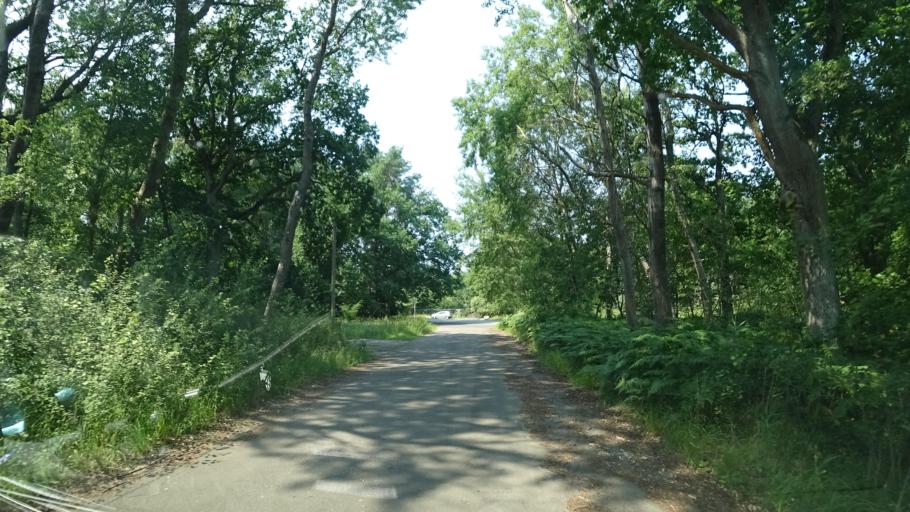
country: DE
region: Mecklenburg-Vorpommern
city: Karlshagen
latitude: 54.1495
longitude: 13.7943
